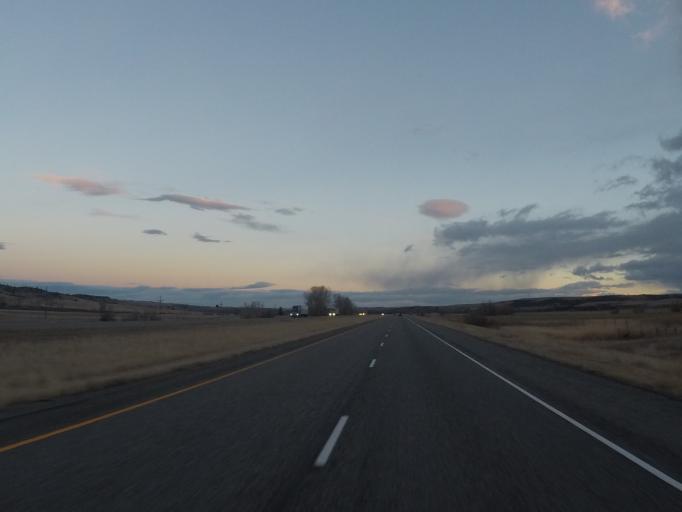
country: US
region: Montana
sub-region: Sweet Grass County
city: Big Timber
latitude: 45.8108
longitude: -109.8626
